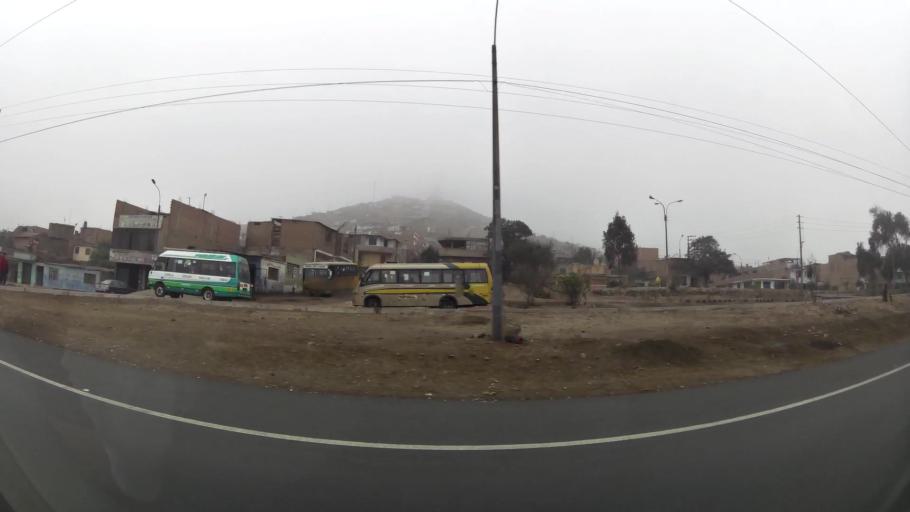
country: PE
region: Lima
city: Ventanilla
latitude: -11.8272
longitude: -77.1208
